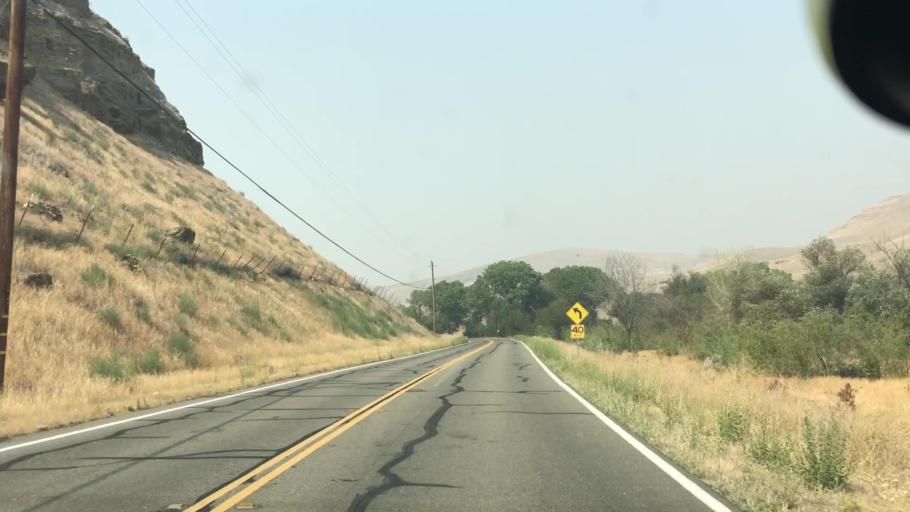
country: US
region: California
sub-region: San Joaquin County
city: Tracy
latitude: 37.6380
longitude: -121.4926
